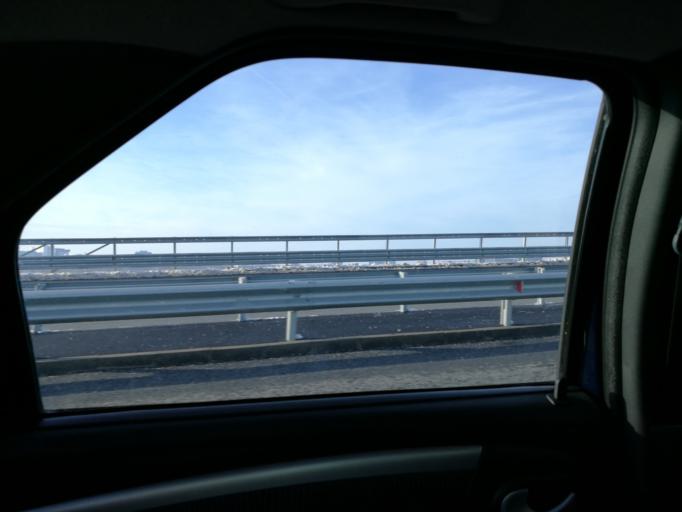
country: RO
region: Ilfov
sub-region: Comuna Fundeni-Dobroesti
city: Fundeni
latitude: 44.4813
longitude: 26.1383
